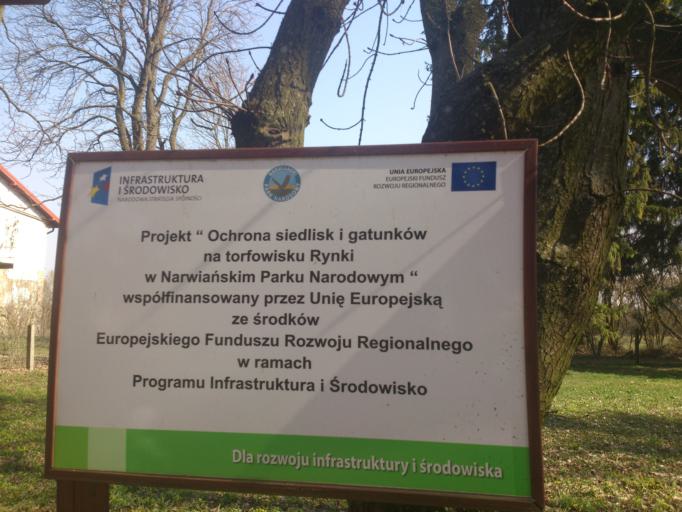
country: PL
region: Podlasie
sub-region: Powiat bialostocki
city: Tykocin
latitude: 53.1054
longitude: 22.7951
